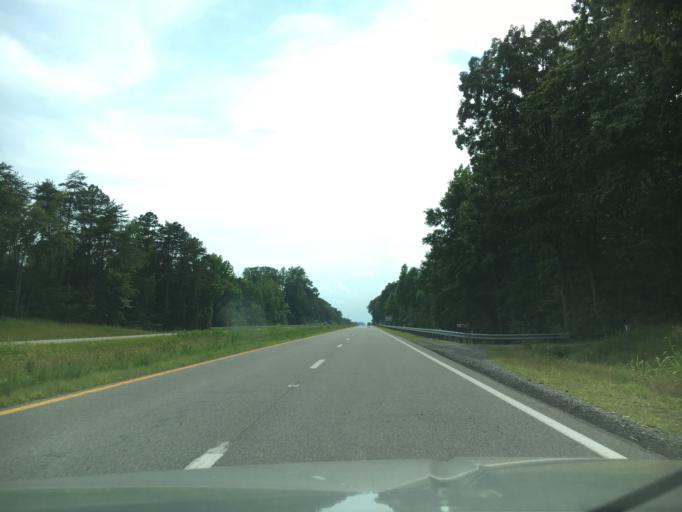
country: US
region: Virginia
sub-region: Mecklenburg County
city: Chase City
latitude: 36.8354
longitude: -78.6526
